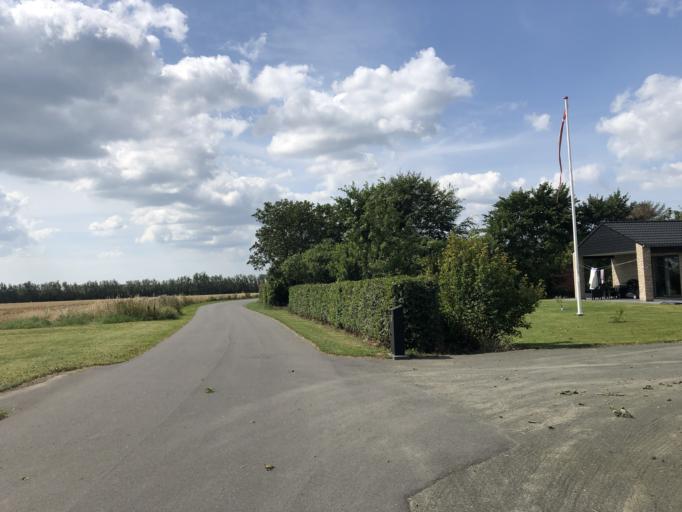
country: DK
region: South Denmark
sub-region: Varde Kommune
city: Oksbol
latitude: 55.8395
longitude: 8.3009
